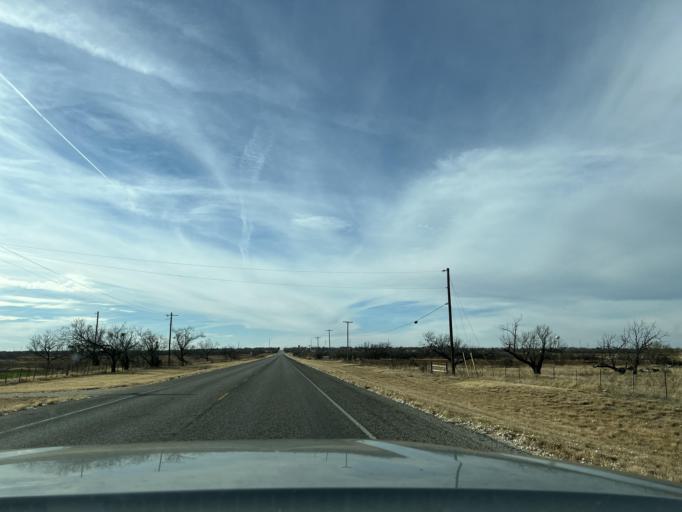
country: US
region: Texas
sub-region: Jones County
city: Anson
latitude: 32.7515
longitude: -99.8769
